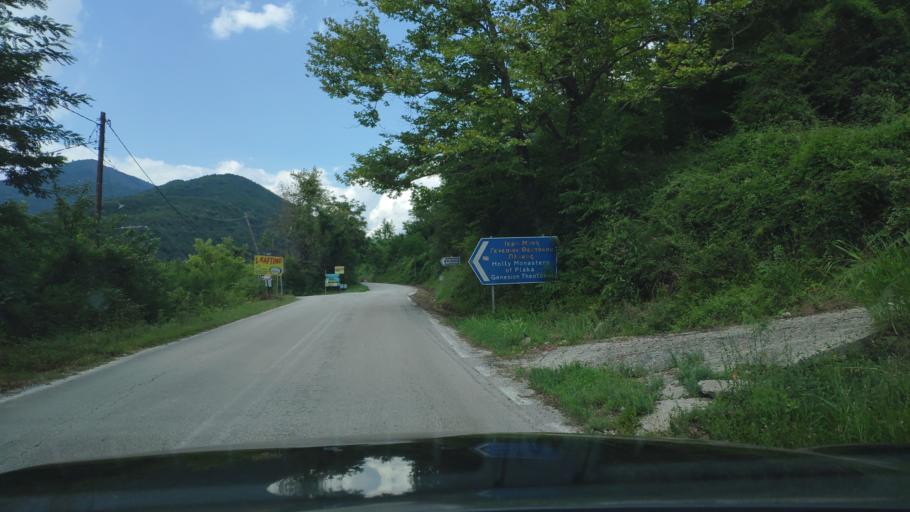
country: GR
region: Epirus
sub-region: Nomos Artas
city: Agios Dimitrios
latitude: 39.4563
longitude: 21.0346
